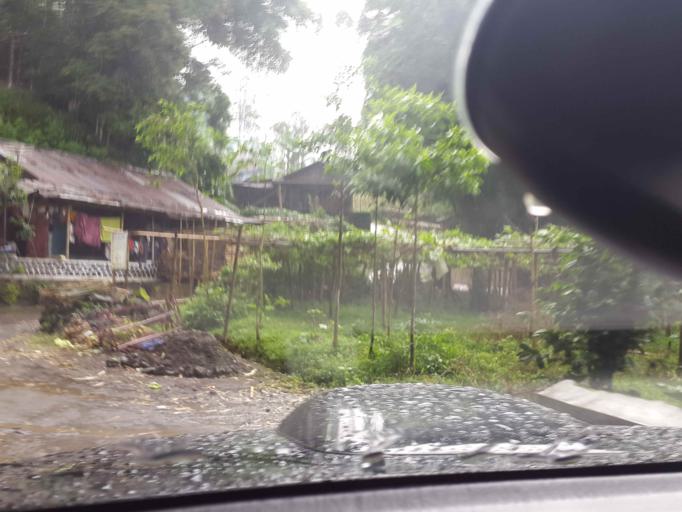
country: ID
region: Central Java
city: Wonosobo
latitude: -7.3636
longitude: 110.0161
